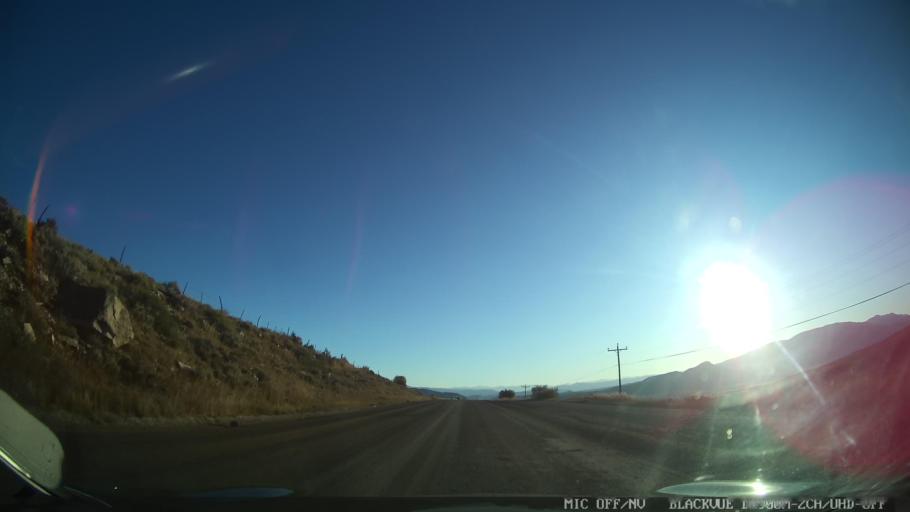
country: US
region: Colorado
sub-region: Grand County
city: Kremmling
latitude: 39.9892
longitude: -106.4258
